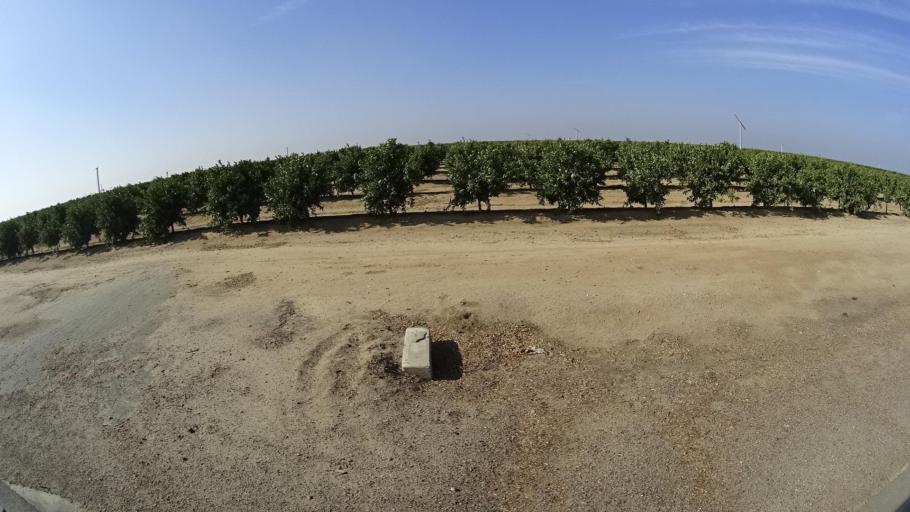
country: US
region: California
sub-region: Kern County
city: McFarland
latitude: 35.6223
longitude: -119.1333
